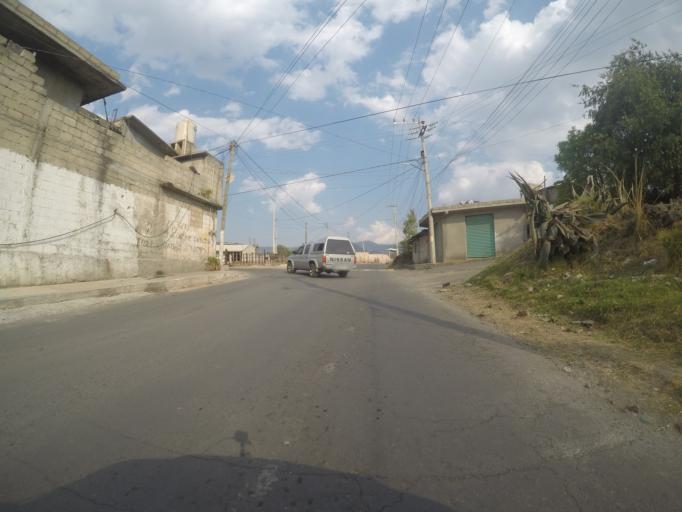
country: MX
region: Mexico
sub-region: Xalatlaco
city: Techichili
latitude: 19.1739
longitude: -99.4202
